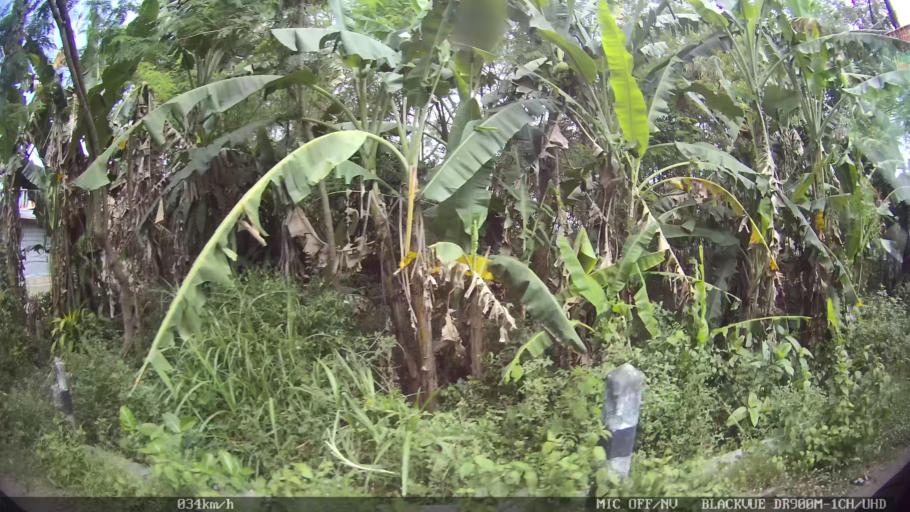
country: ID
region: Central Java
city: Candi Prambanan
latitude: -7.7348
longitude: 110.4725
